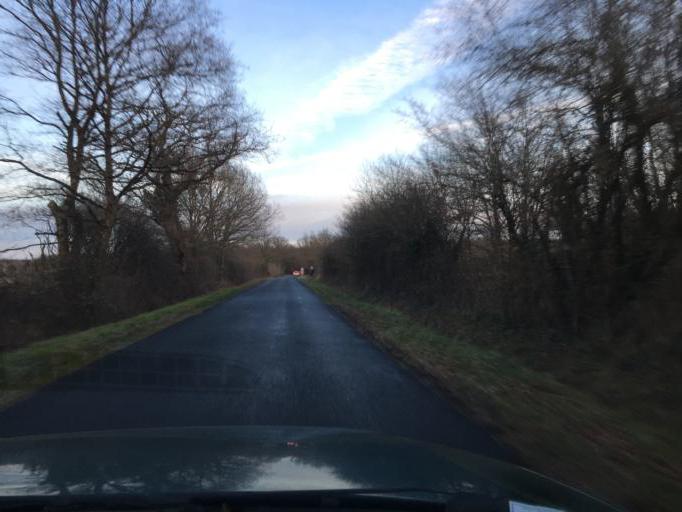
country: FR
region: Centre
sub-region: Departement du Loiret
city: Olivet
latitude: 47.7978
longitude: 1.9035
